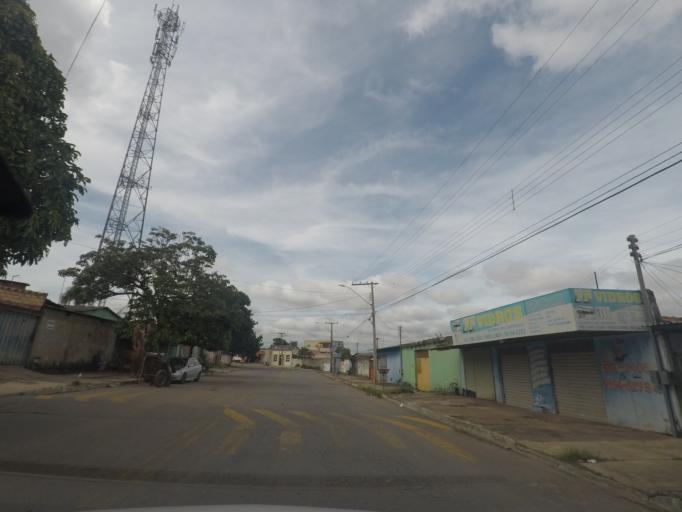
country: BR
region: Goias
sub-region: Goiania
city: Goiania
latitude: -16.6605
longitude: -49.1965
